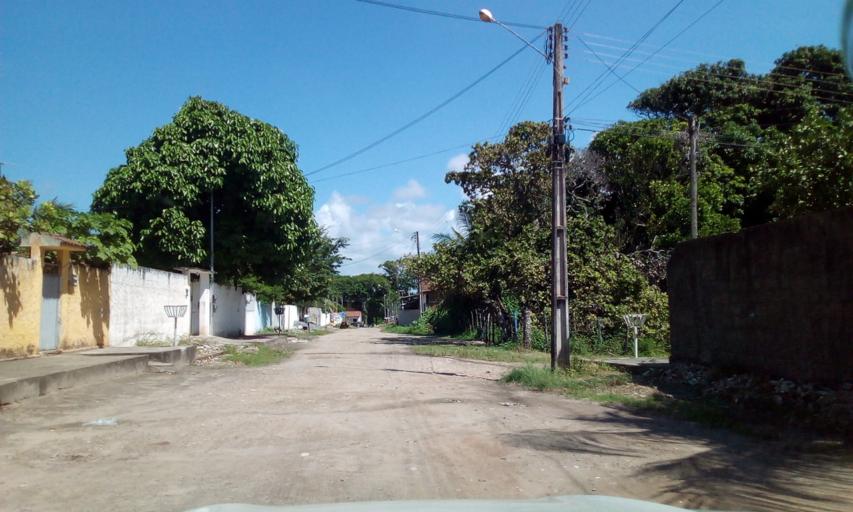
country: BR
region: Paraiba
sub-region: Joao Pessoa
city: Joao Pessoa
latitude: -7.1820
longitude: -34.8184
